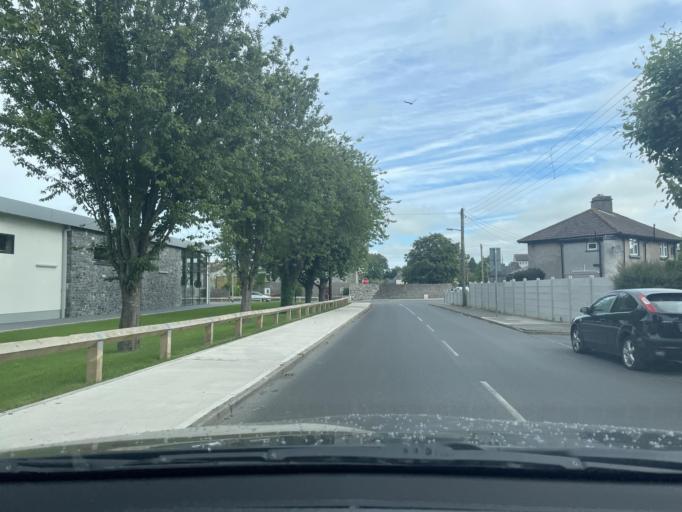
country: IE
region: Leinster
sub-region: County Carlow
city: Bagenalstown
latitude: 52.7000
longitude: -6.9638
